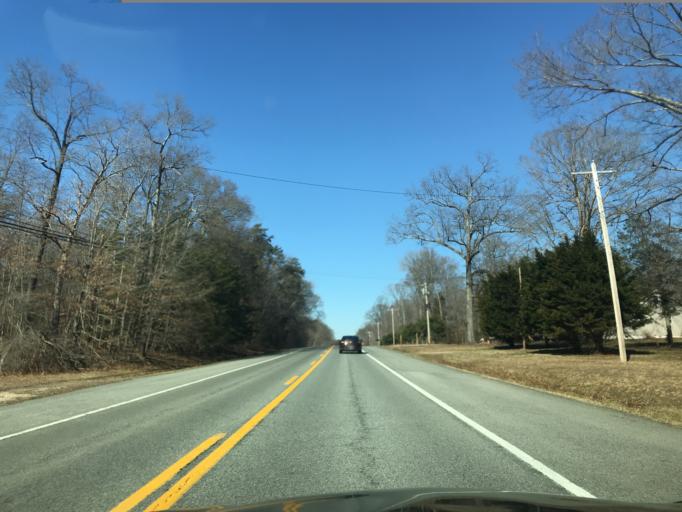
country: US
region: Maryland
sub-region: Charles County
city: Bryans Road
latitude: 38.6551
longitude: -77.0774
